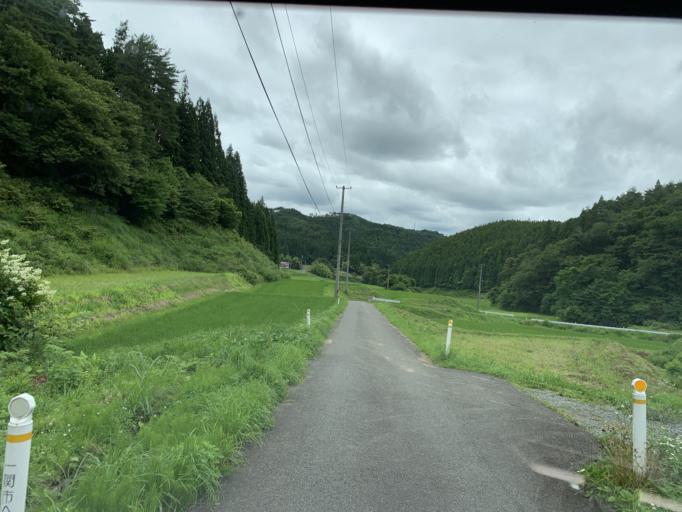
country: JP
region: Iwate
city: Ichinoseki
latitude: 38.8978
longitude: 140.9771
